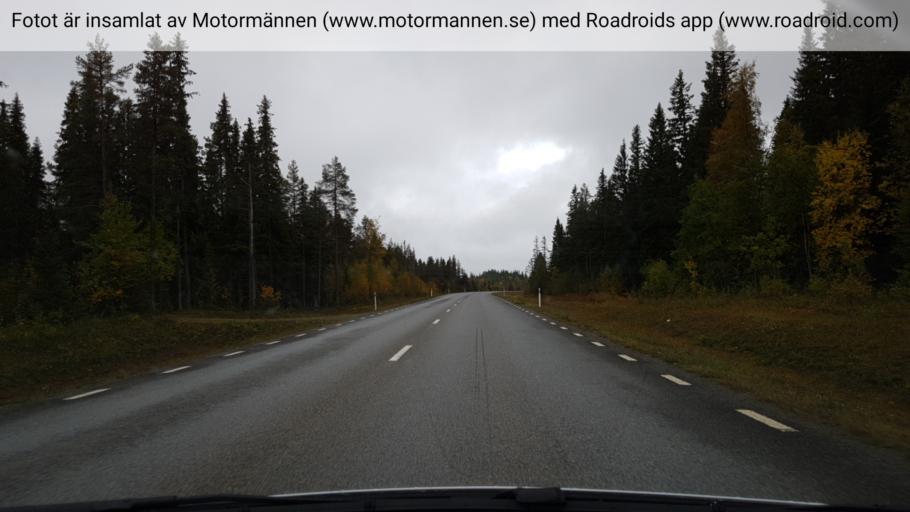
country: SE
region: Jaemtland
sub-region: Stroemsunds Kommun
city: Stroemsund
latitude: 63.7098
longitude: 15.4573
